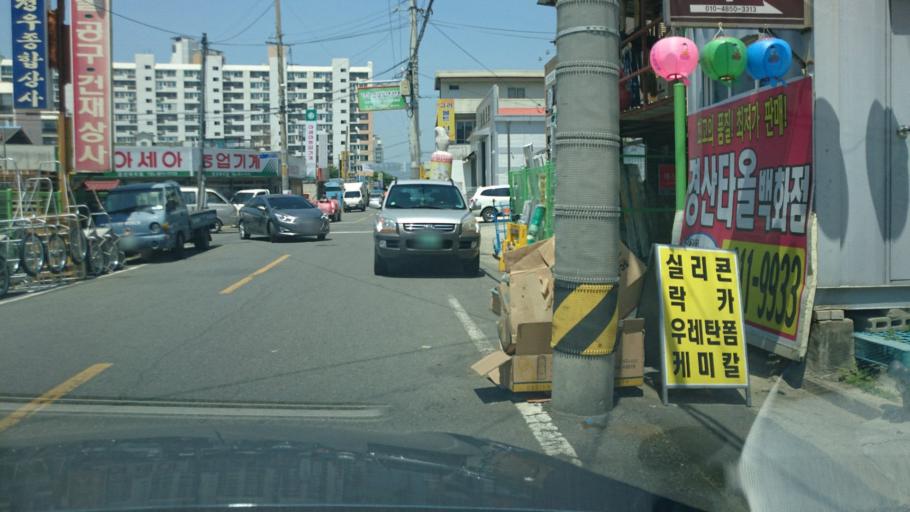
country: KR
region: Gyeongsangbuk-do
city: Gyeongsan-si
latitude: 35.8282
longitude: 128.7384
